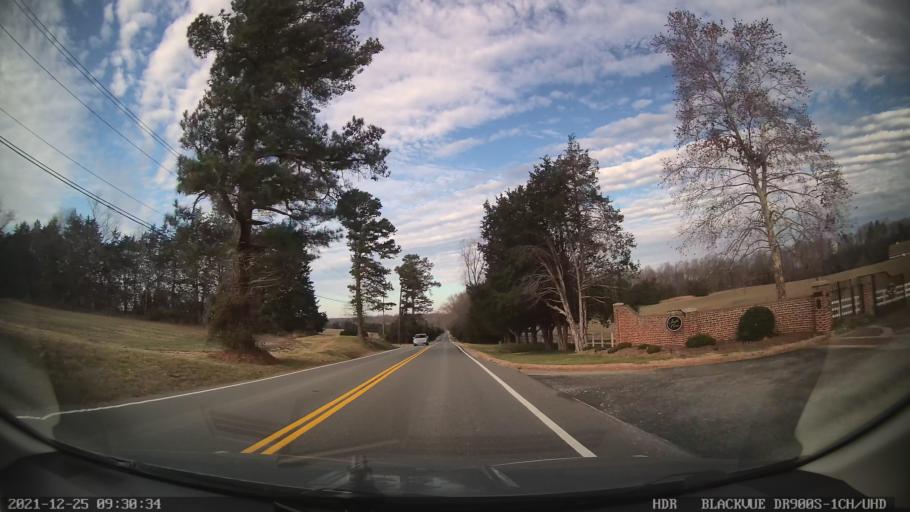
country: US
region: Virginia
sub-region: Goochland County
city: Goochland
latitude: 37.7107
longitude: -77.8065
